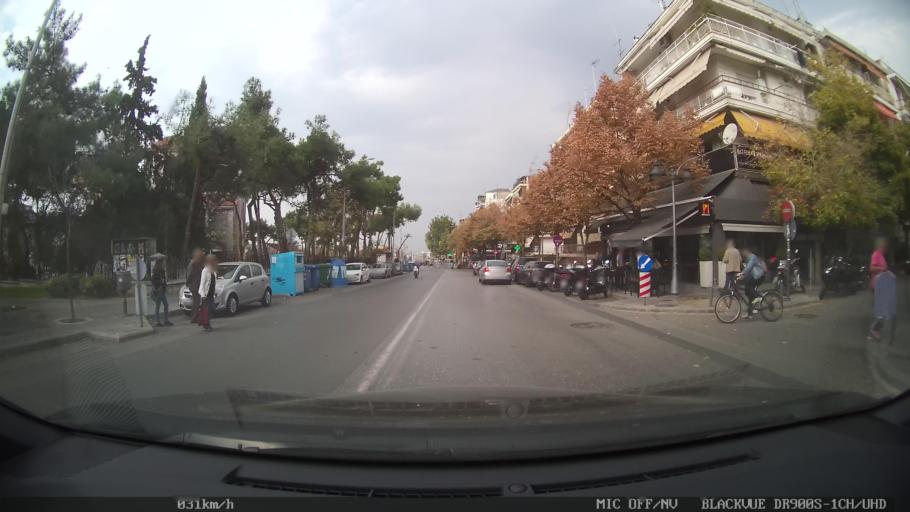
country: GR
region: Central Macedonia
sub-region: Nomos Thessalonikis
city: Triandria
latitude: 40.6158
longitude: 22.9747
